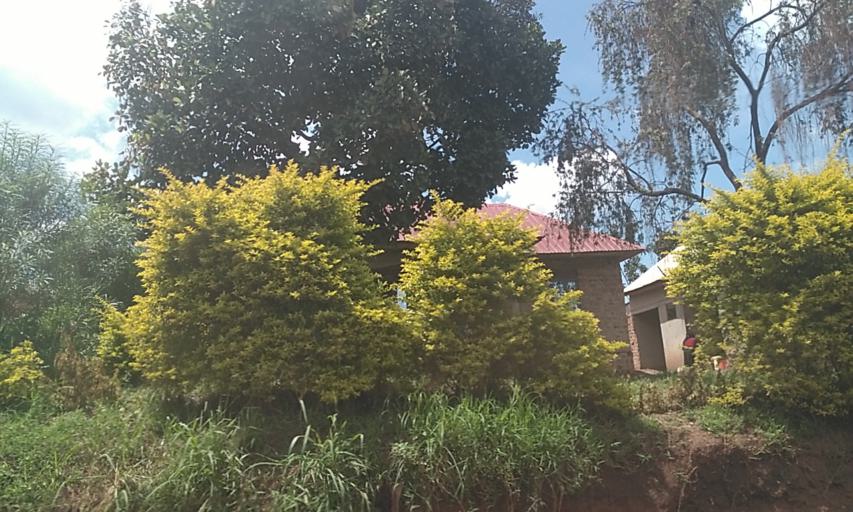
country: UG
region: Central Region
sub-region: Wakiso District
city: Wakiso
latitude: 0.3930
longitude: 32.4648
